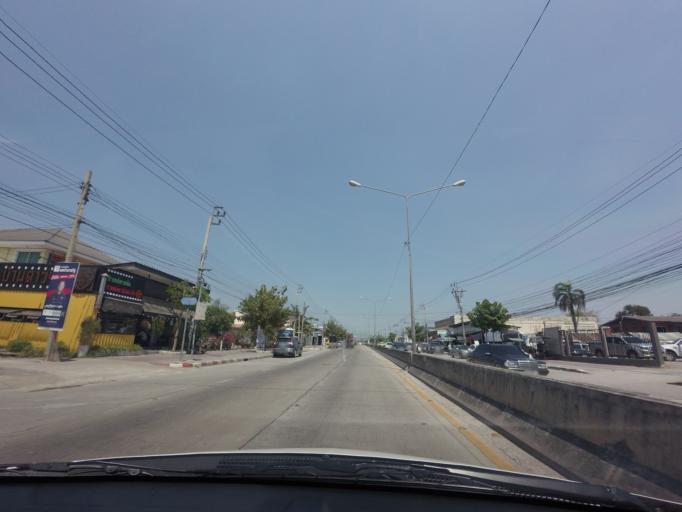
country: TH
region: Bangkok
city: Khlong Sam Wa
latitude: 13.8355
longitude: 100.7773
